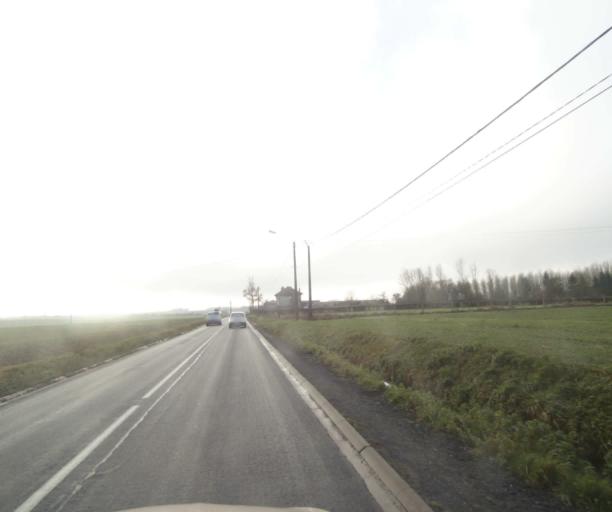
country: FR
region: Nord-Pas-de-Calais
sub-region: Departement du Nord
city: Famars
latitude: 50.3047
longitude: 3.5172
